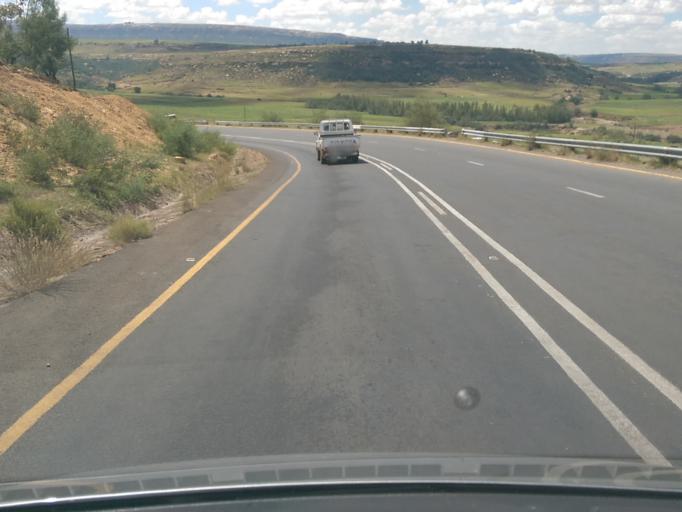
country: LS
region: Maseru
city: Maseru
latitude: -29.4038
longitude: 27.5744
